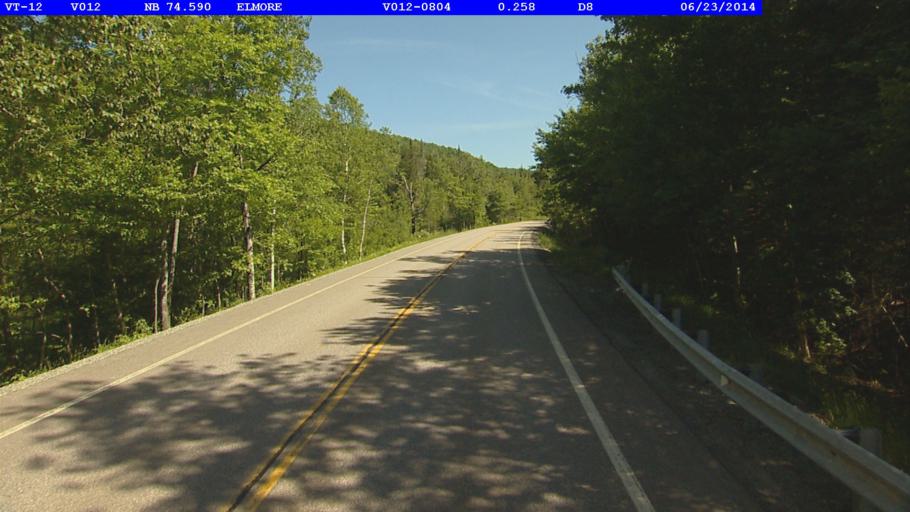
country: US
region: Vermont
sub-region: Lamoille County
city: Morrisville
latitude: 44.4558
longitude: -72.5472
